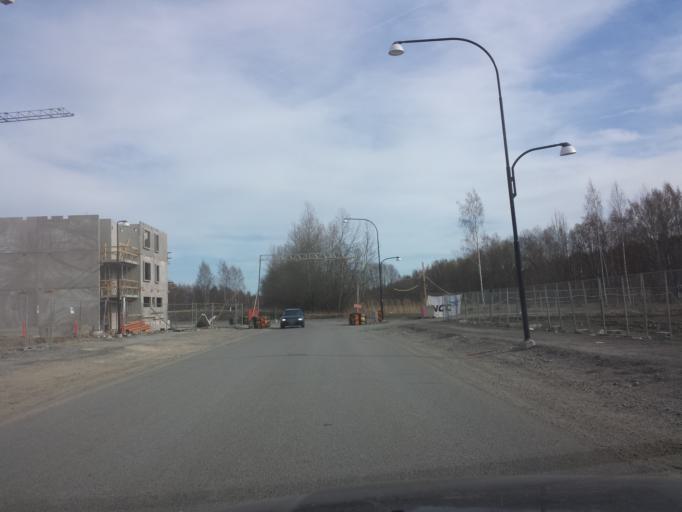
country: SE
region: OErebro
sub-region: Orebro Kommun
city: Orebro
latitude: 59.2520
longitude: 15.2212
